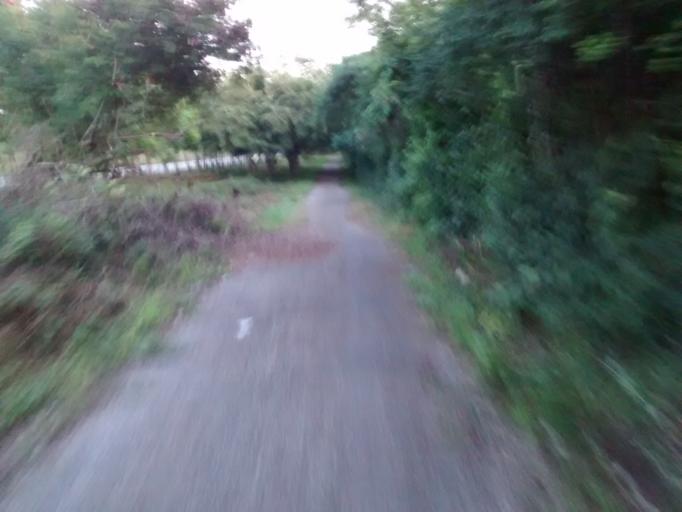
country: MX
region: Yucatan
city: Valladolid
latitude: 20.6947
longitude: -88.2280
